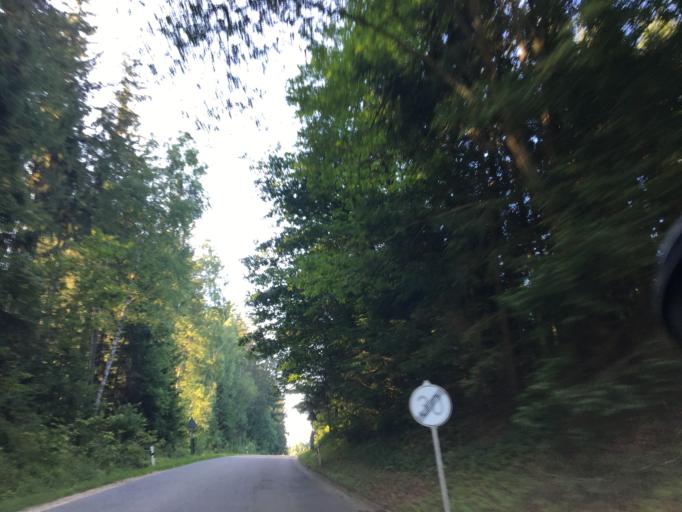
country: DE
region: Bavaria
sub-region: Lower Bavaria
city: Geisenhausen
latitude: 48.4603
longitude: 12.2777
